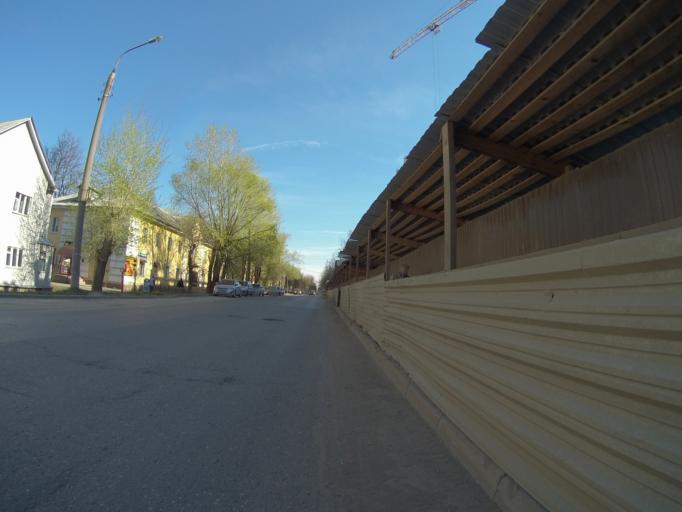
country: RU
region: Vladimir
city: Vladimir
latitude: 56.1466
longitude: 40.4166
